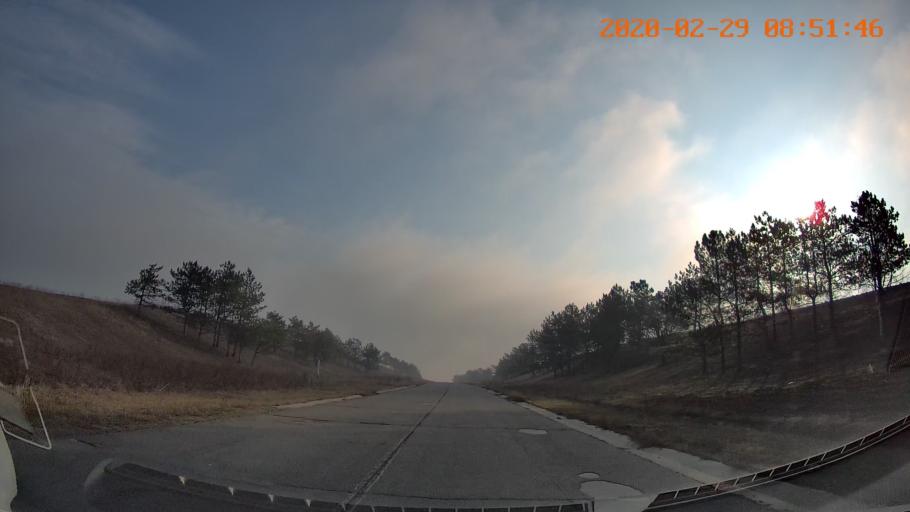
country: MD
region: Anenii Noi
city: Varnita
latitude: 46.9224
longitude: 29.5263
